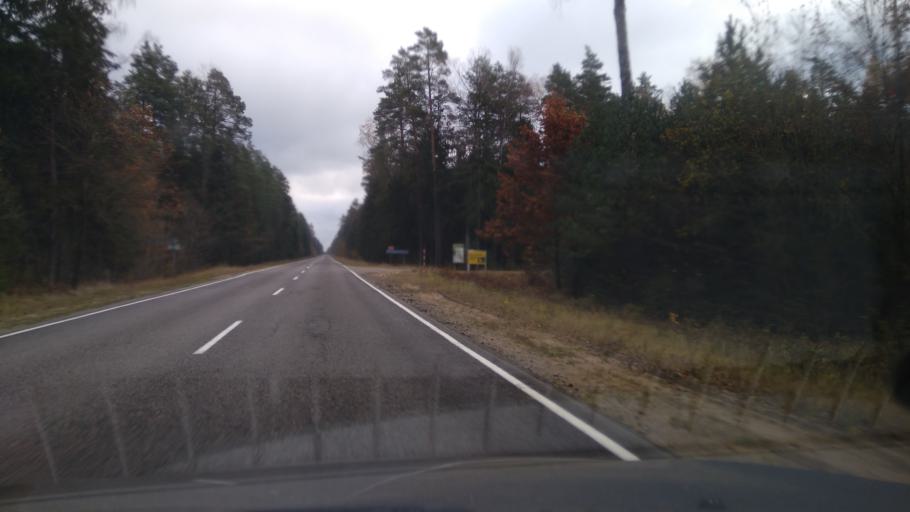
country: BY
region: Minsk
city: Urechcha
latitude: 53.2148
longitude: 27.8620
